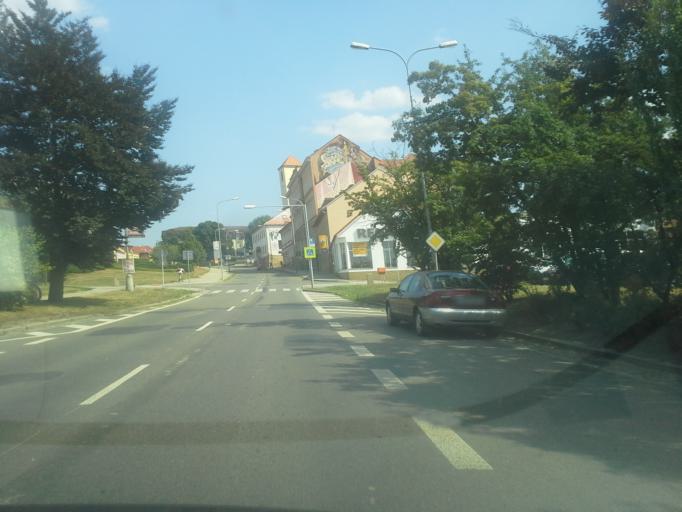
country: CZ
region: South Moravian
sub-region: Okres Blansko
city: Boskovice
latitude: 49.4894
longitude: 16.6556
